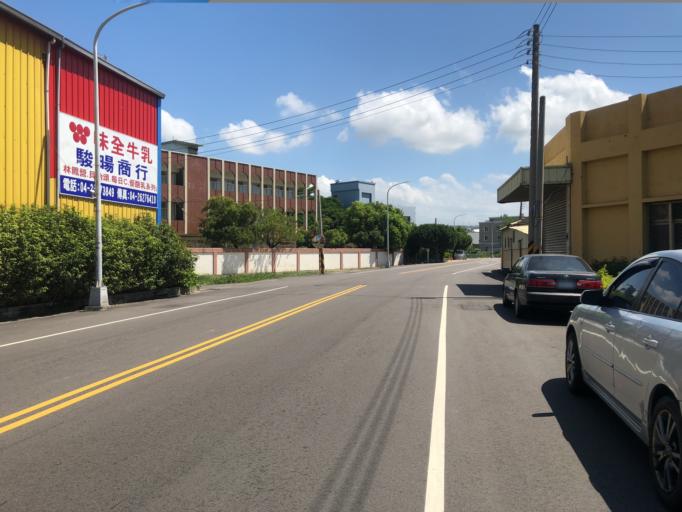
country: TW
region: Taiwan
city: Fengyuan
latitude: 24.2801
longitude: 120.5594
